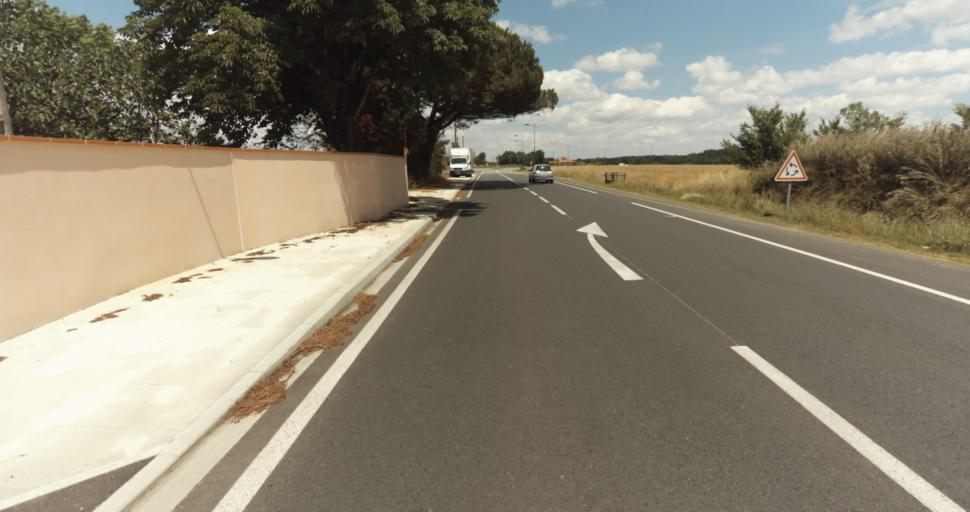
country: FR
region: Midi-Pyrenees
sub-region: Departement de la Haute-Garonne
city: Fontenilles
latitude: 43.5384
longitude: 1.1874
